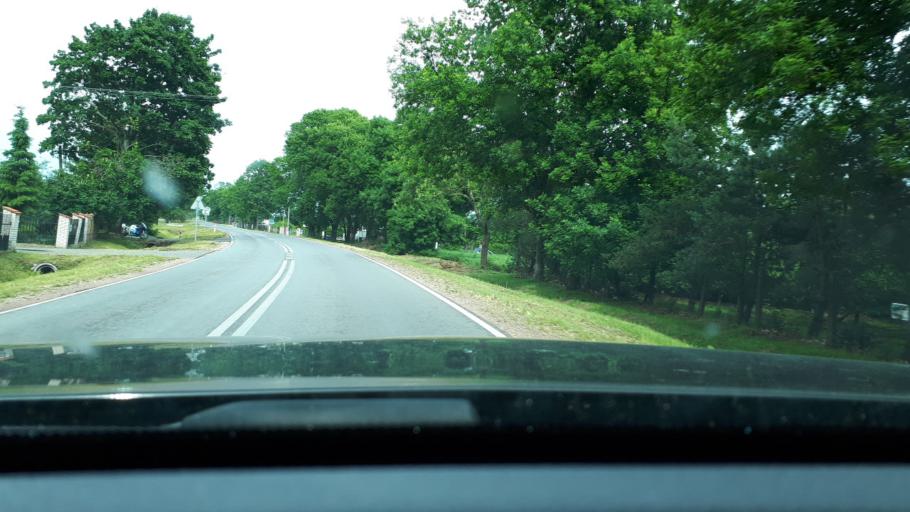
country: PL
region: Masovian Voivodeship
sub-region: Powiat sochaczewski
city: Teresin
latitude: 52.2609
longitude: 20.3585
